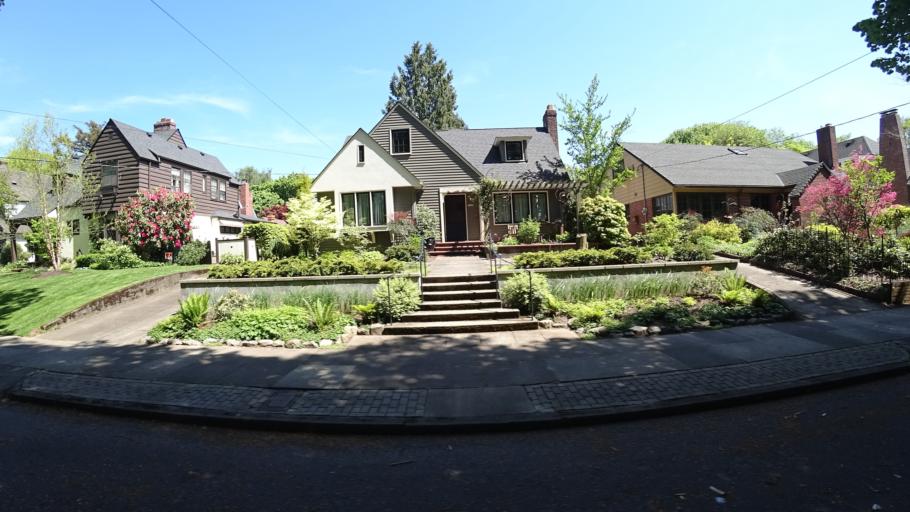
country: US
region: Oregon
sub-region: Clackamas County
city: Milwaukie
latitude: 45.4715
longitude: -122.6293
